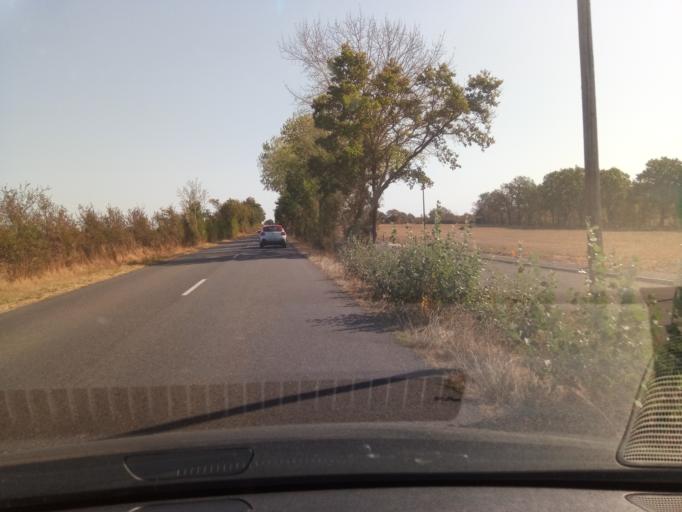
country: FR
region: Poitou-Charentes
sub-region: Departement de la Vienne
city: Montmorillon
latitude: 46.4336
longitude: 0.9017
